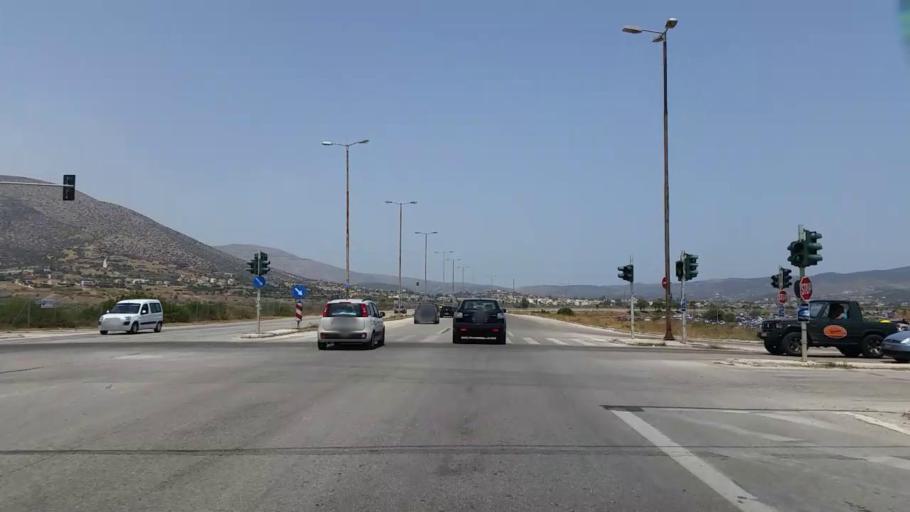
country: GR
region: Attica
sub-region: Nomarchia Anatolikis Attikis
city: Anavyssos
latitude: 37.7244
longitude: 23.9319
